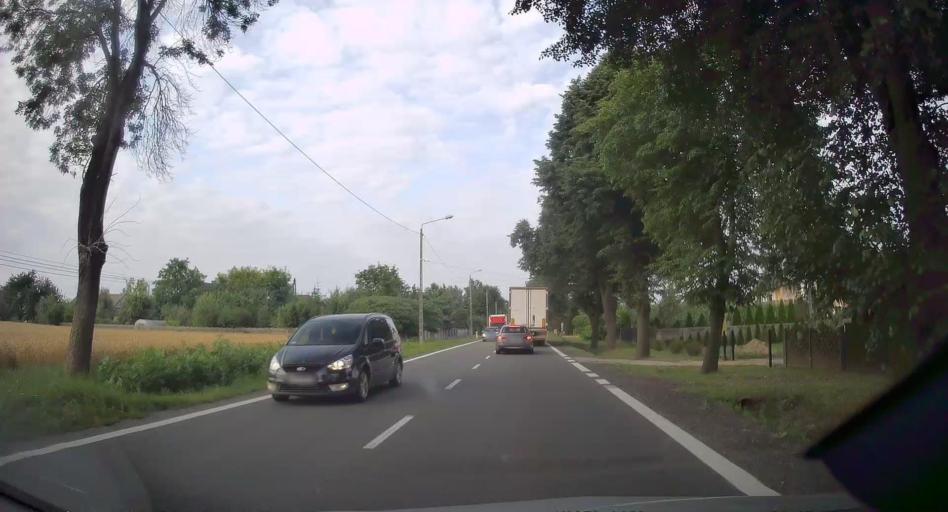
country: PL
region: Silesian Voivodeship
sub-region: Powiat czestochowski
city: Borowno
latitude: 50.9089
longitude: 19.3016
